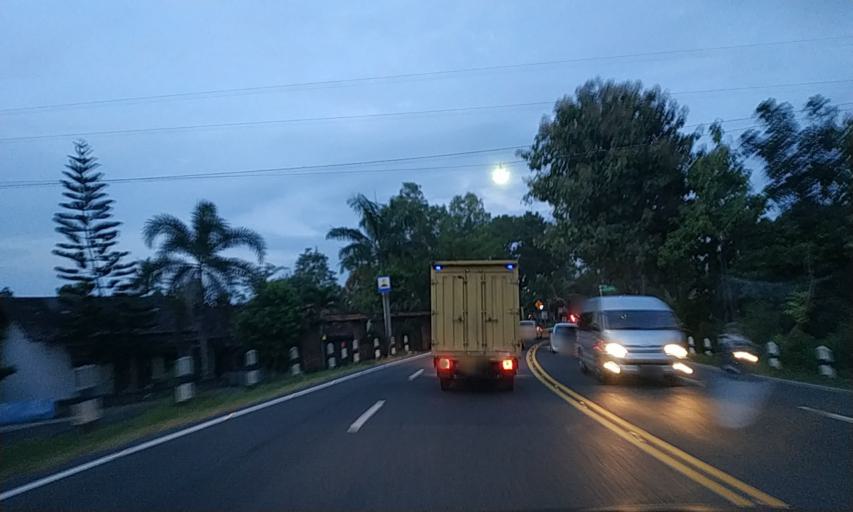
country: ID
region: Daerah Istimewa Yogyakarta
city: Godean
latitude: -7.8279
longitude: 110.2221
